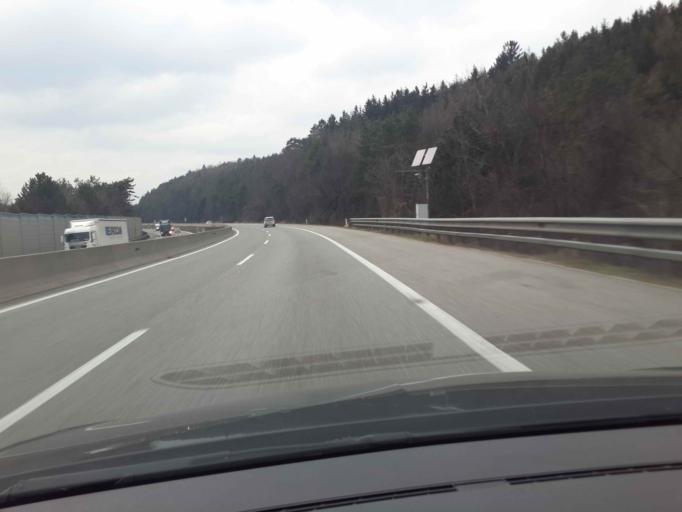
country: AT
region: Lower Austria
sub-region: Politischer Bezirk Baden
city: Klausen-Leopoldsdorf
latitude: 48.0952
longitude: 15.9926
